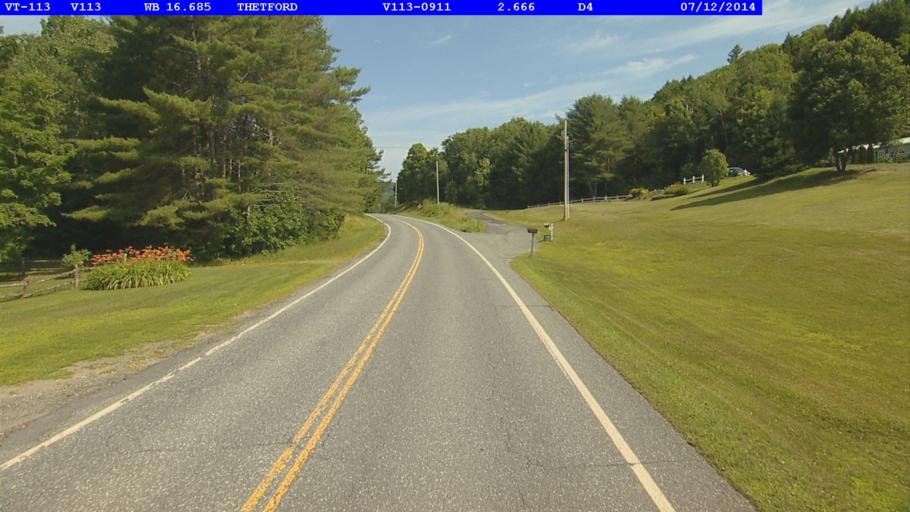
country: US
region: New Hampshire
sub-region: Grafton County
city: Lyme
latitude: 43.8605
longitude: -72.2600
